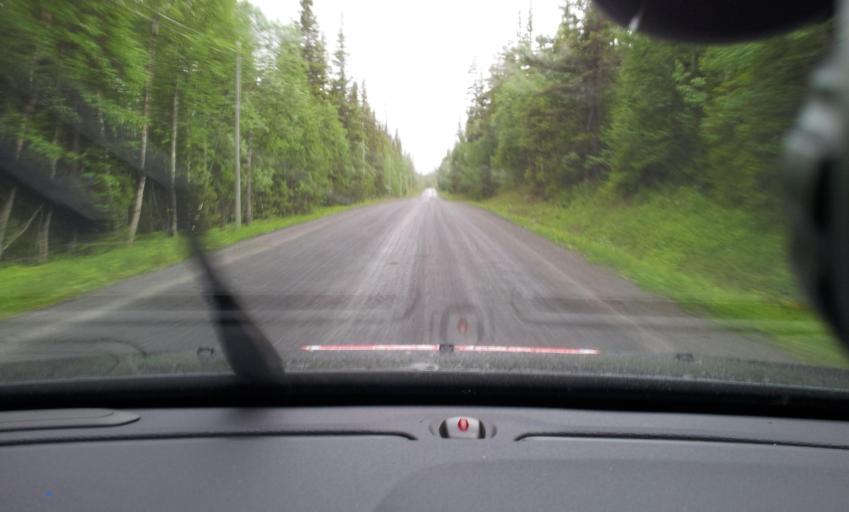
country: SE
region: Jaemtland
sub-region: Are Kommun
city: Are
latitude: 63.1599
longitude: 13.0478
